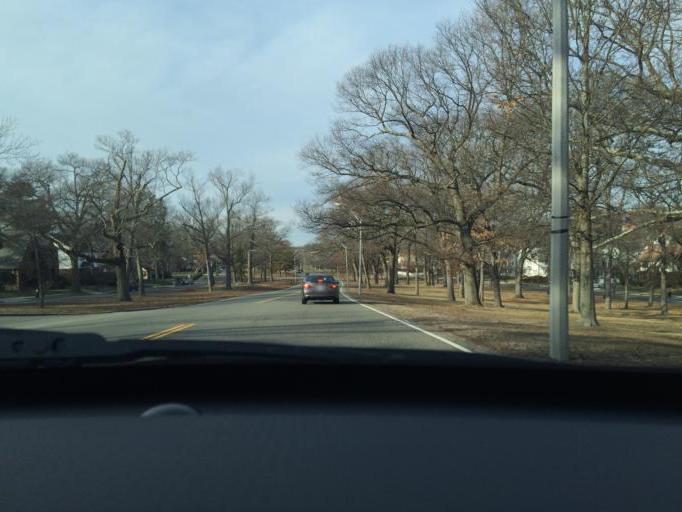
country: US
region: Massachusetts
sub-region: Suffolk County
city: Jamaica Plain
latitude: 42.2787
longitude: -71.1423
